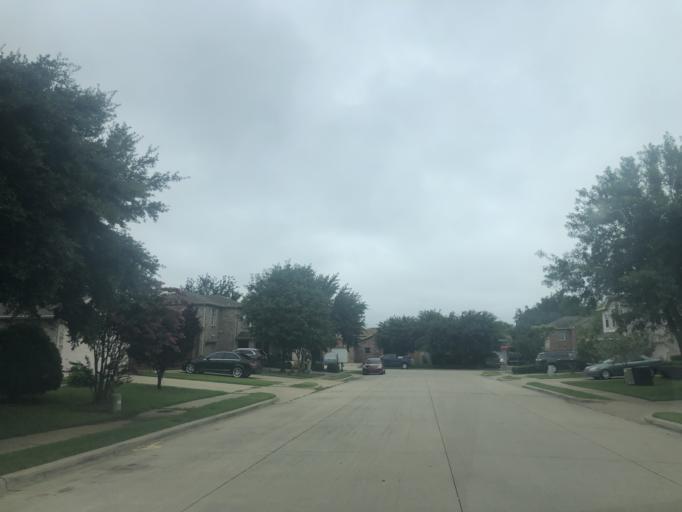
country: US
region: Texas
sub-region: Dallas County
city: Dallas
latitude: 32.7904
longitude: -96.8613
